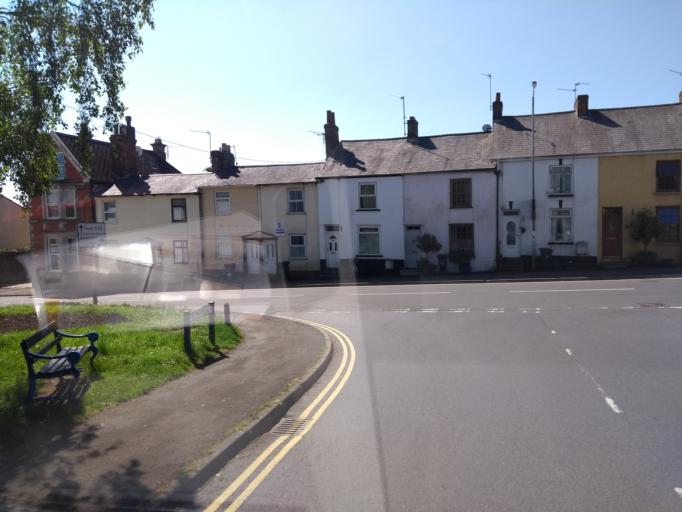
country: GB
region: England
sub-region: Somerset
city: Chard
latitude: 50.8726
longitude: -2.9700
